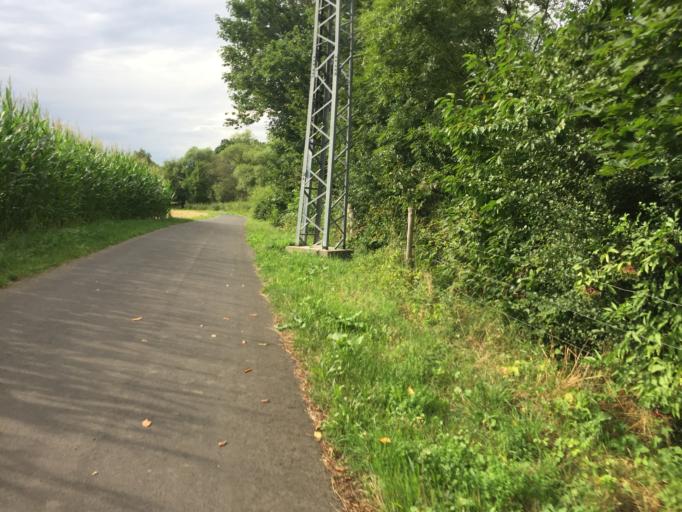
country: DE
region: Hesse
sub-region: Regierungsbezirk Kassel
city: Rotenburg an der Fulda
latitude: 51.0042
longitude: 9.7121
